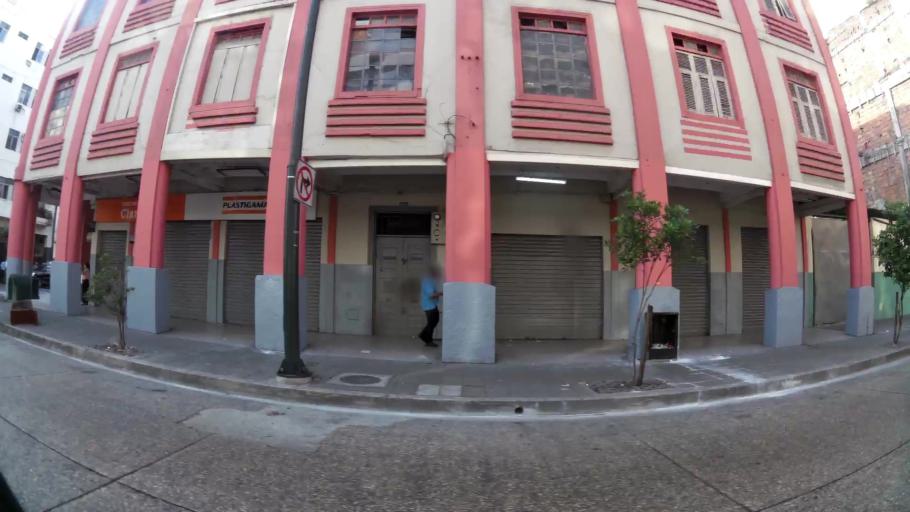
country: EC
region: Guayas
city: Guayaquil
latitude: -2.1922
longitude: -79.8864
